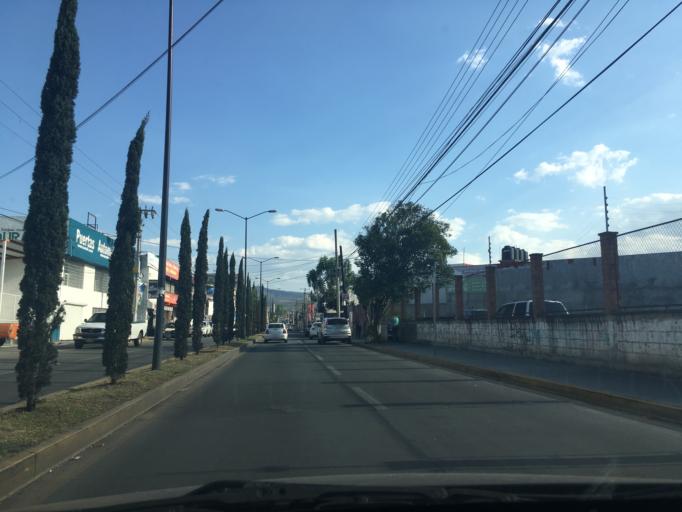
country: MX
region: Michoacan
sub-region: Morelia
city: Morelos
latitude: 19.6825
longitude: -101.2258
